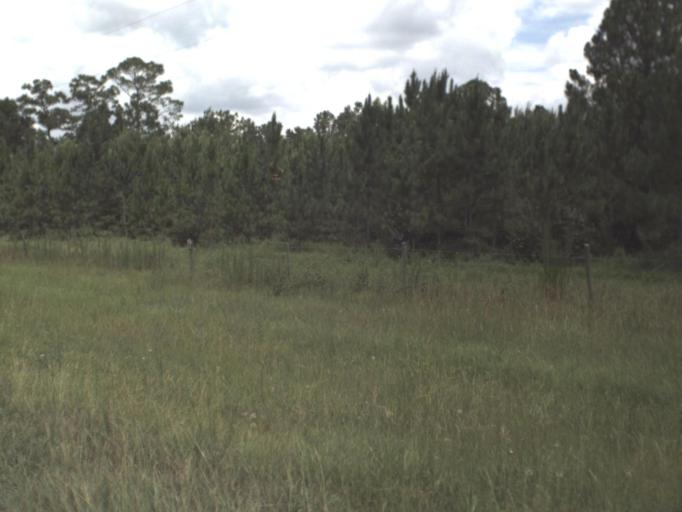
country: US
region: Florida
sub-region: Union County
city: Lake Butler
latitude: 29.9138
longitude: -82.3964
